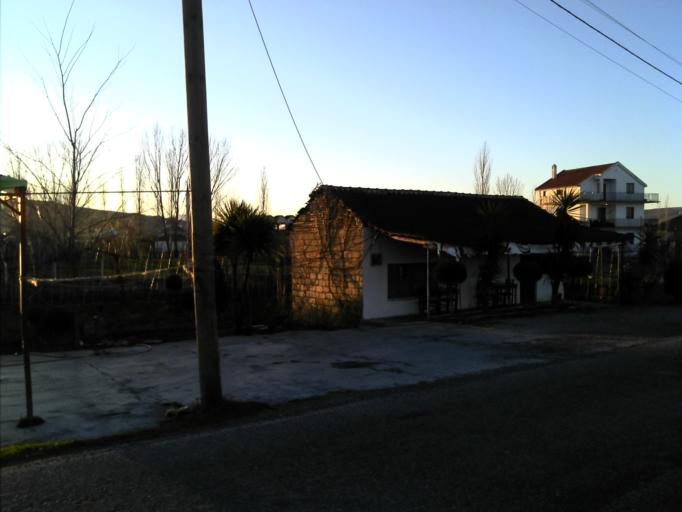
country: AL
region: Shkoder
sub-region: Rrethi i Shkodres
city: Berdica e Madhe
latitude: 41.9822
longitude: 19.4803
